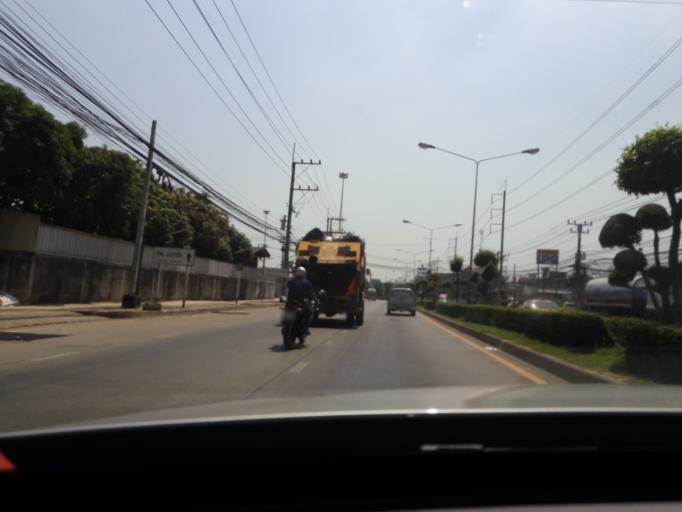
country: TH
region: Samut Sakhon
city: Samut Sakhon
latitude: 13.5641
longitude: 100.2720
